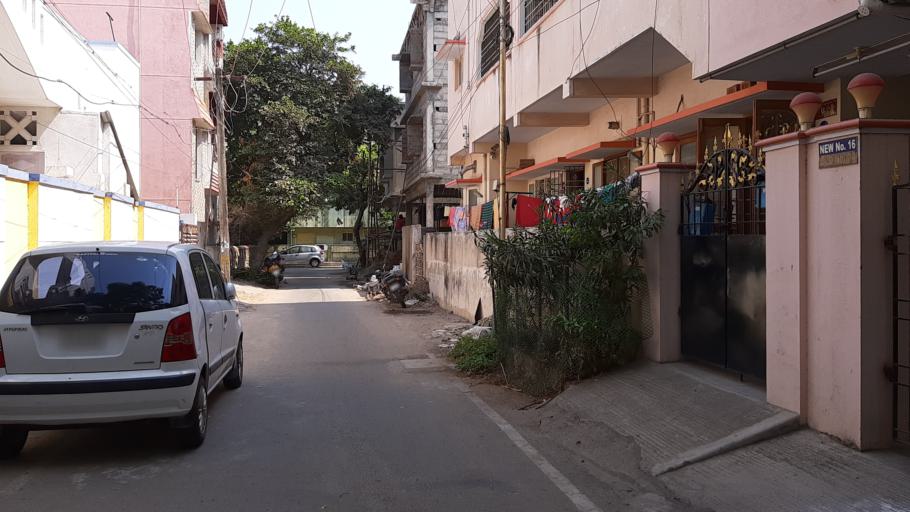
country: IN
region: Tamil Nadu
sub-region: Kancheepuram
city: Alandur
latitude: 12.9960
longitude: 80.2058
